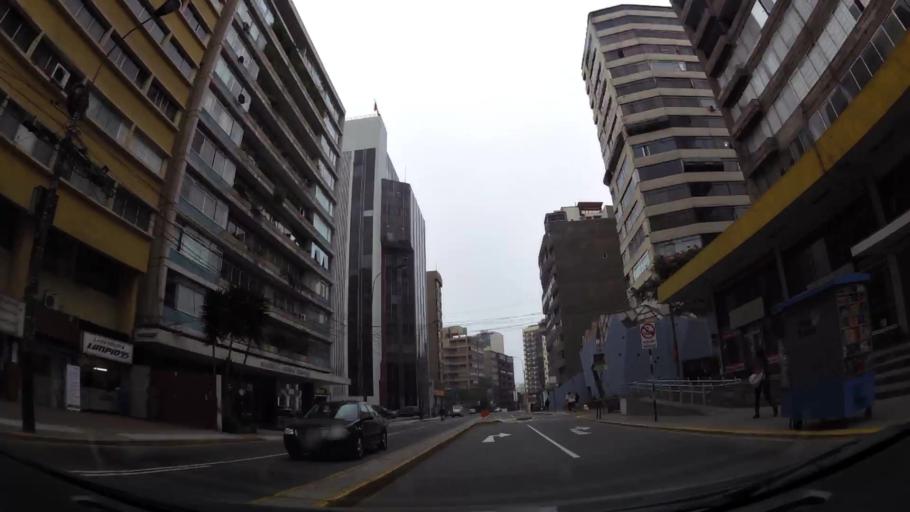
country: PE
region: Lima
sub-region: Lima
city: San Isidro
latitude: -12.1242
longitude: -77.0304
